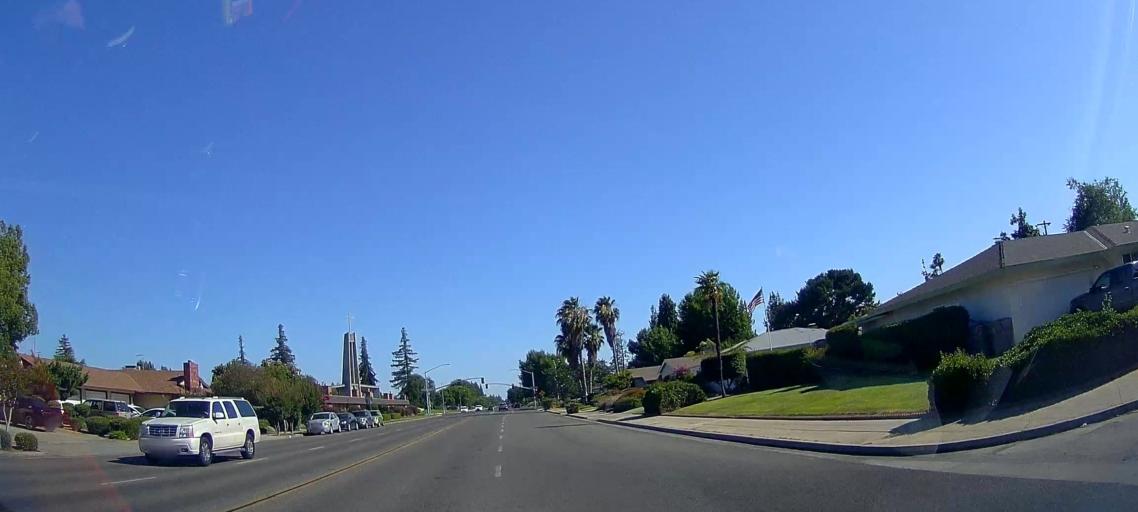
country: US
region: California
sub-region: Fresno County
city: Fresno
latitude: 36.8242
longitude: -119.7994
